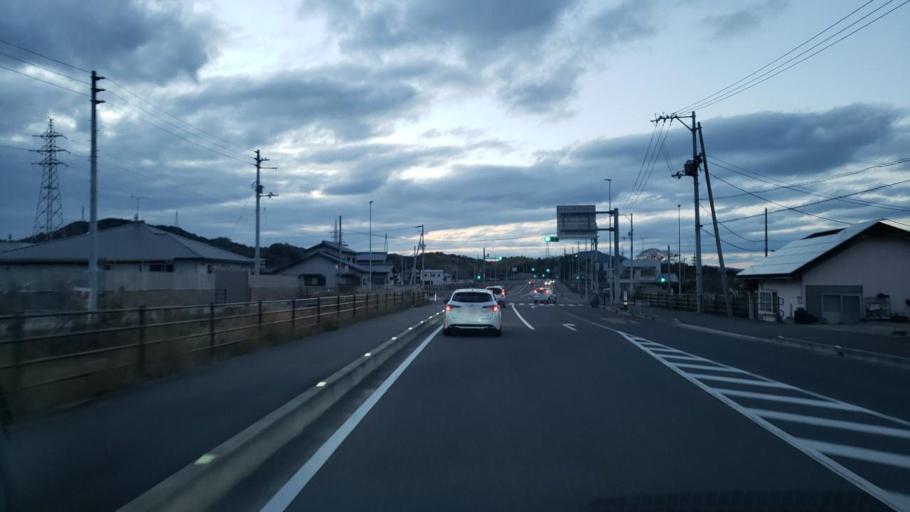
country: JP
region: Tokushima
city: Kamojimacho-jogejima
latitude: 34.2406
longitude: 134.3513
